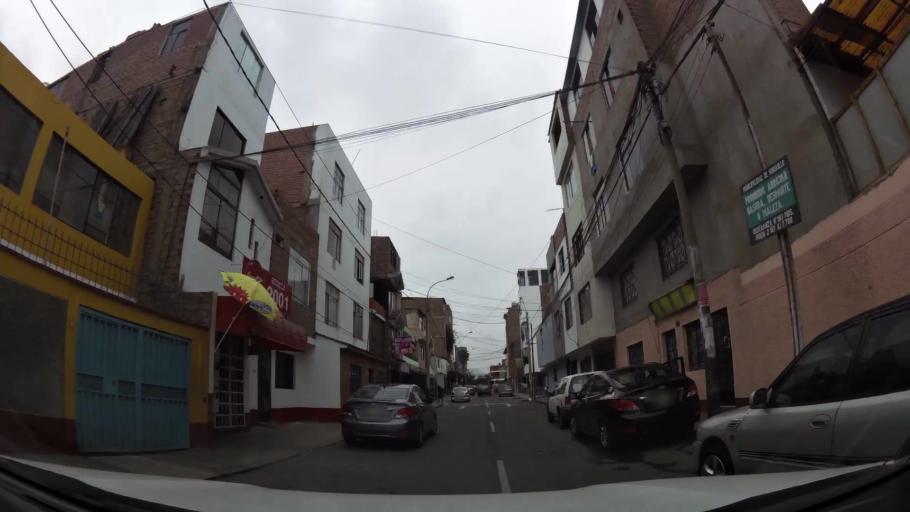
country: PE
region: Lima
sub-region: Lima
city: Surco
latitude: -12.1081
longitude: -77.0115
